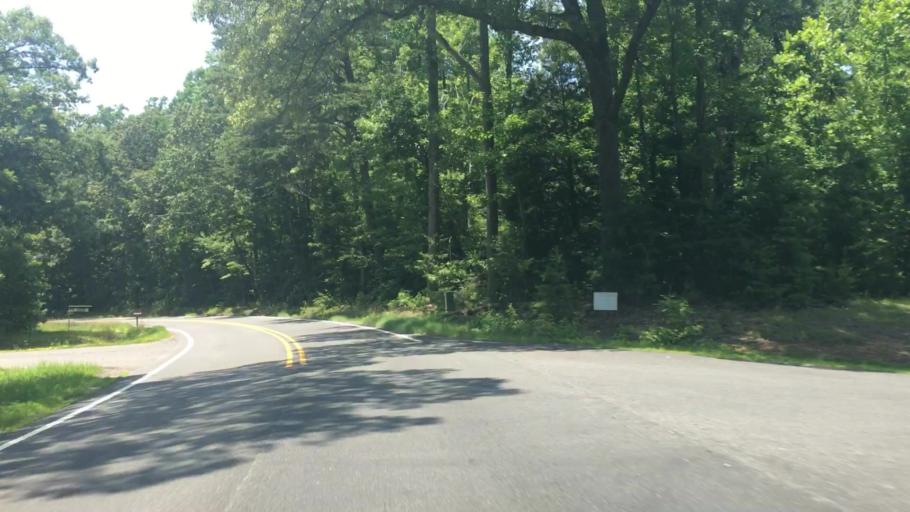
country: US
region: Virginia
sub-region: King George County
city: King George
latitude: 38.3184
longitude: -77.1942
